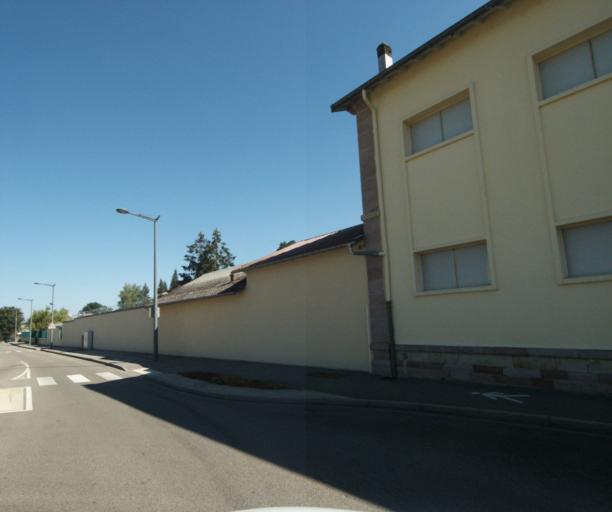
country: FR
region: Lorraine
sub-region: Departement des Vosges
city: Chantraine
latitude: 48.1562
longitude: 6.4584
